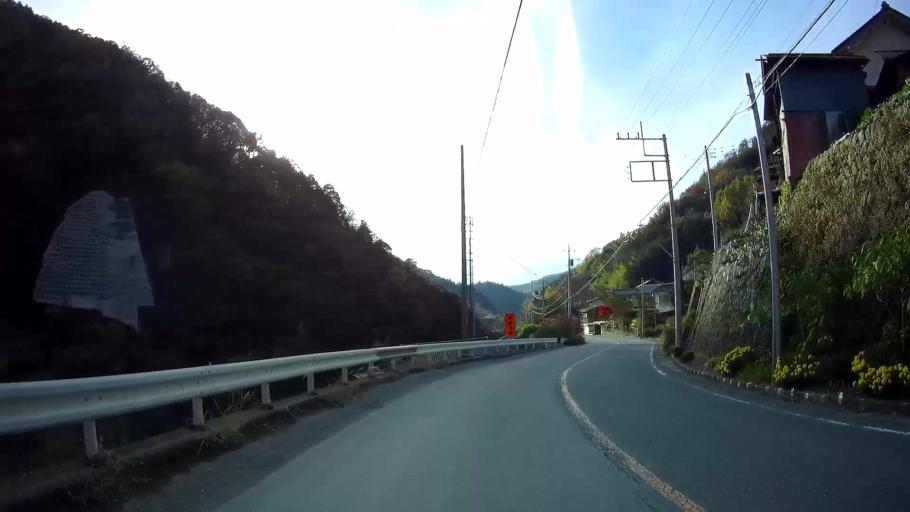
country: JP
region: Yamanashi
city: Fujikawaguchiko
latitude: 35.4749
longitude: 138.5383
